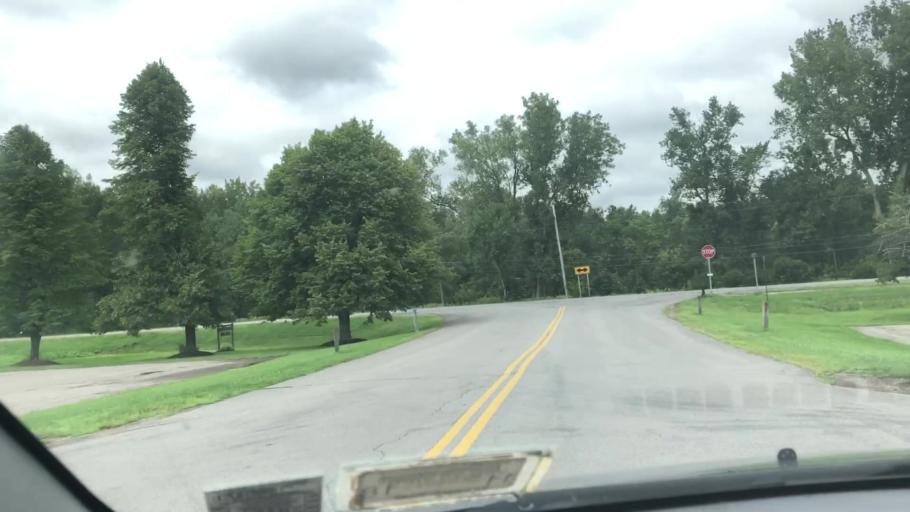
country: US
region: New York
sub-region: Wayne County
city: Macedon
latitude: 43.1386
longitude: -77.2864
